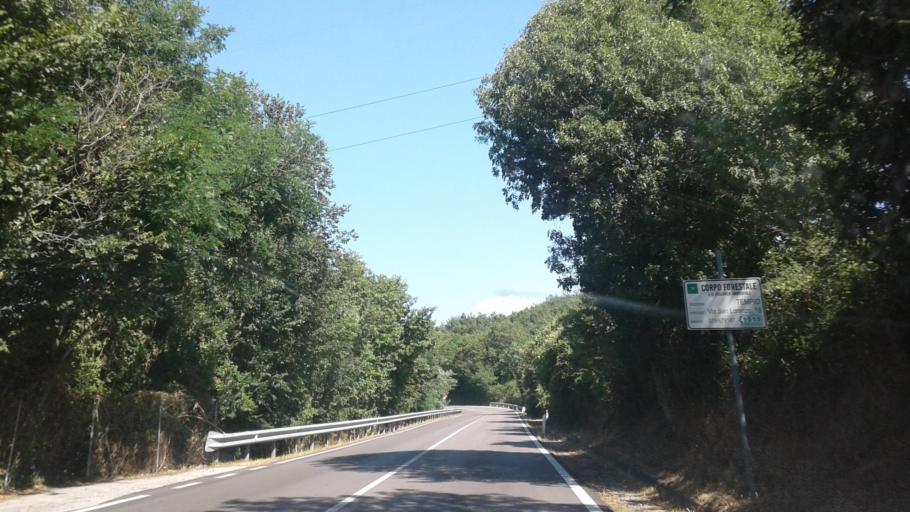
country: IT
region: Sardinia
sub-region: Provincia di Olbia-Tempio
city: Tempio Pausania
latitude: 40.9076
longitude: 9.0890
